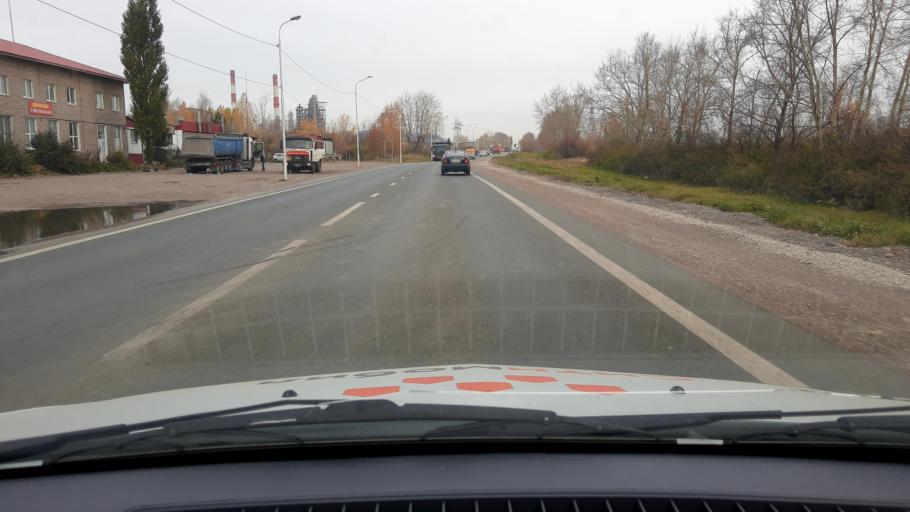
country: RU
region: Bashkortostan
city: Ufa
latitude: 54.8466
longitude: 56.1196
